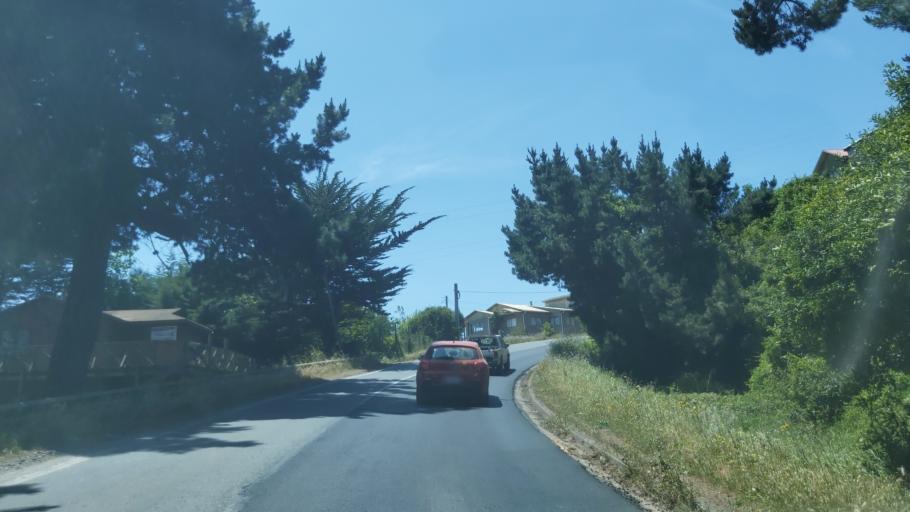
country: CL
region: Maule
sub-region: Provincia de Cauquenes
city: Cauquenes
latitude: -35.8256
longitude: -72.6089
